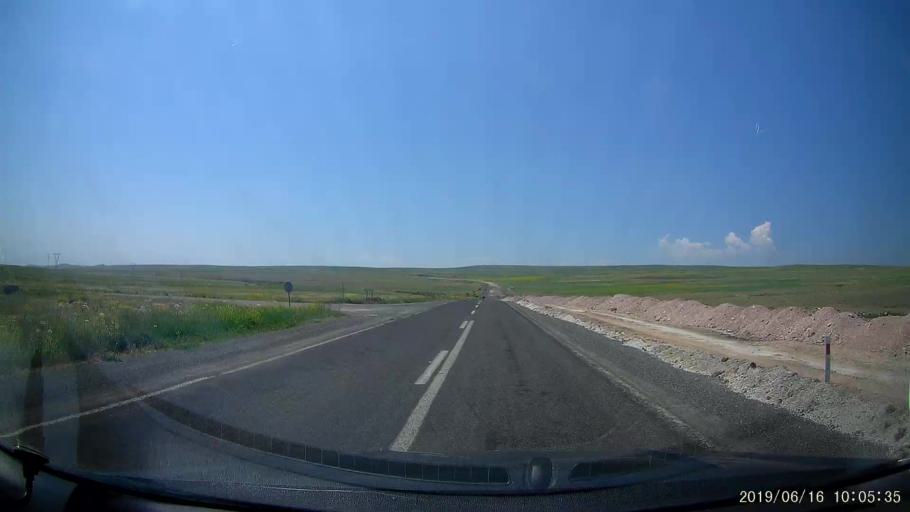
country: TR
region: Kars
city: Digor
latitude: 40.2678
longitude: 43.5389
